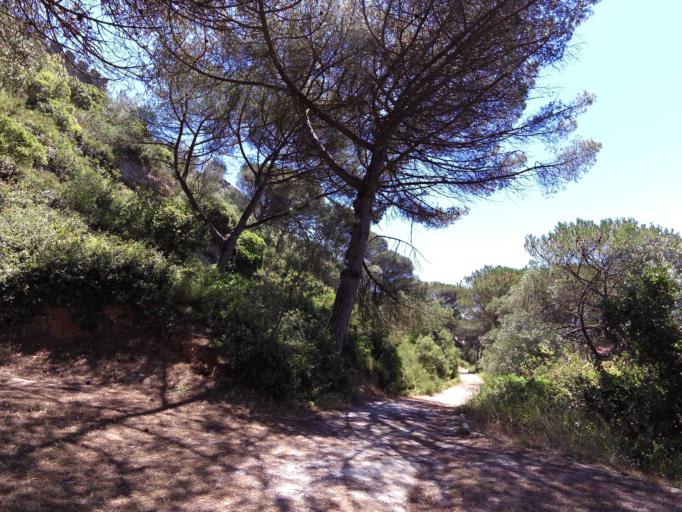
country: PT
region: Leiria
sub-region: Obidos
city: Obidos
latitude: 39.3597
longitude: -9.1590
